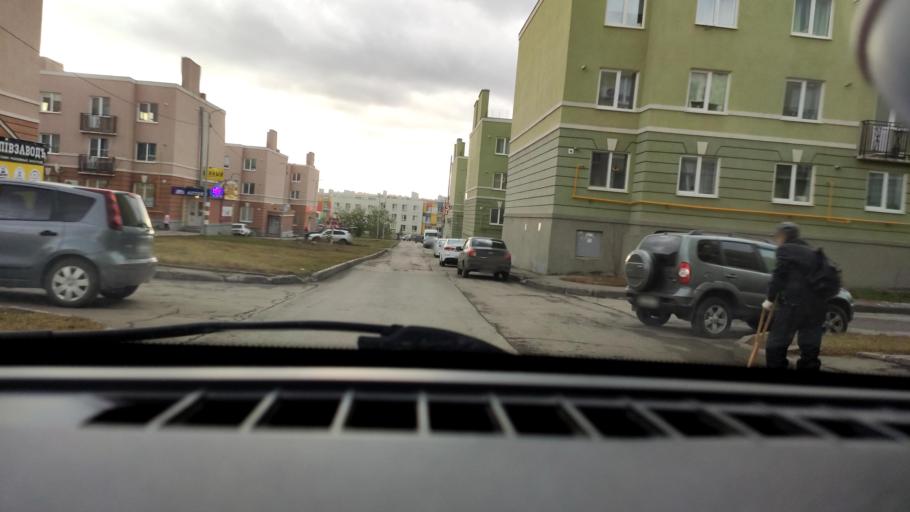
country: RU
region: Samara
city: Petra-Dubrava
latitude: 53.3160
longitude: 50.3087
